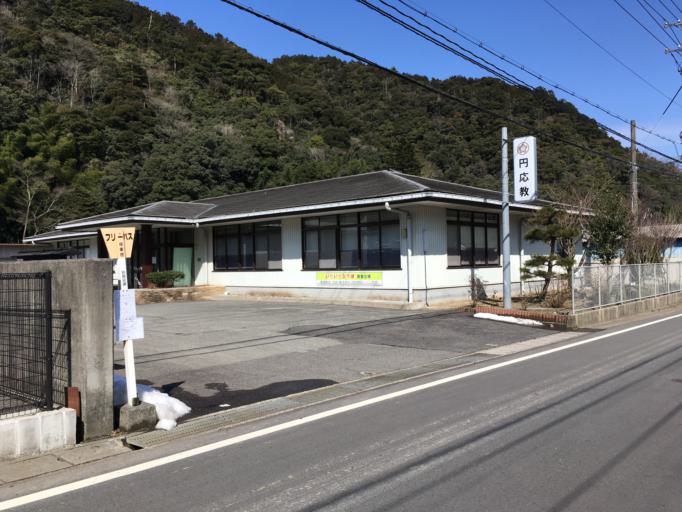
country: JP
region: Shimane
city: Masuda
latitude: 34.4530
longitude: 131.7642
